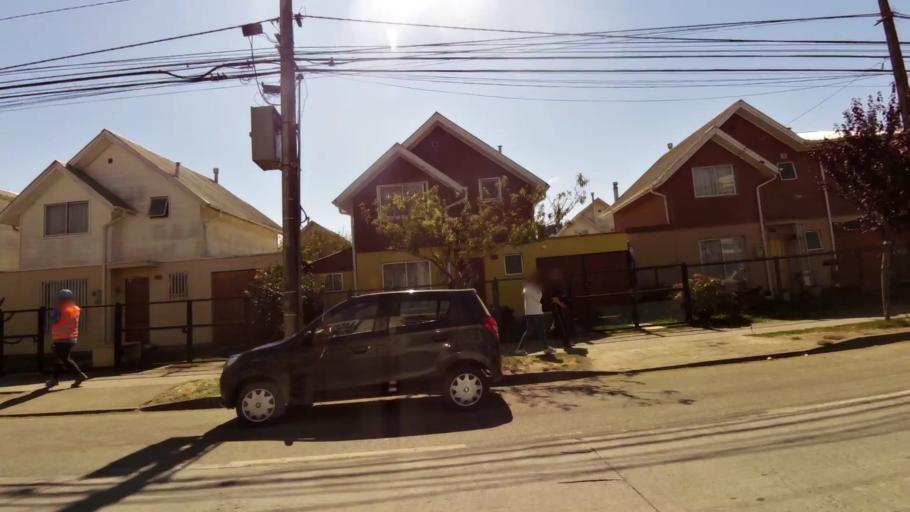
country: CL
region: Biobio
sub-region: Provincia de Concepcion
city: Concepcion
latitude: -36.7902
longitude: -73.0348
